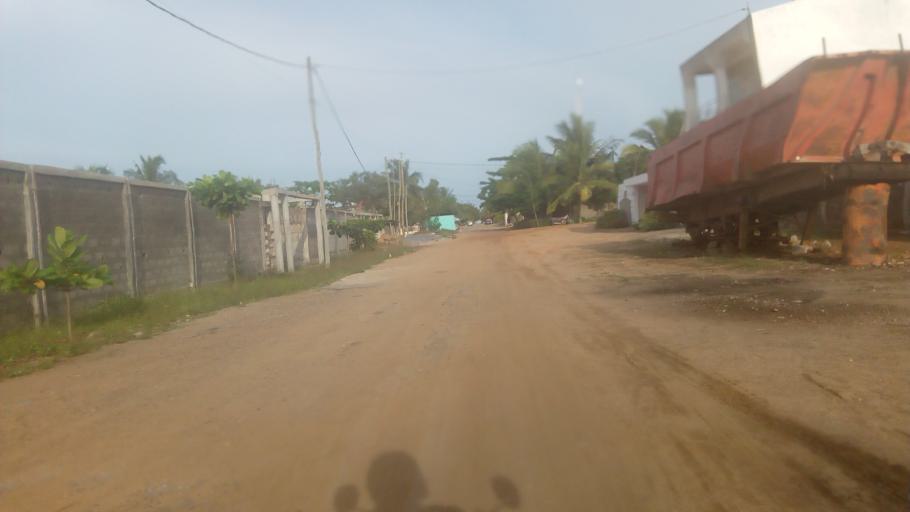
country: TG
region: Maritime
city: Lome
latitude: 6.1631
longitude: 1.3250
